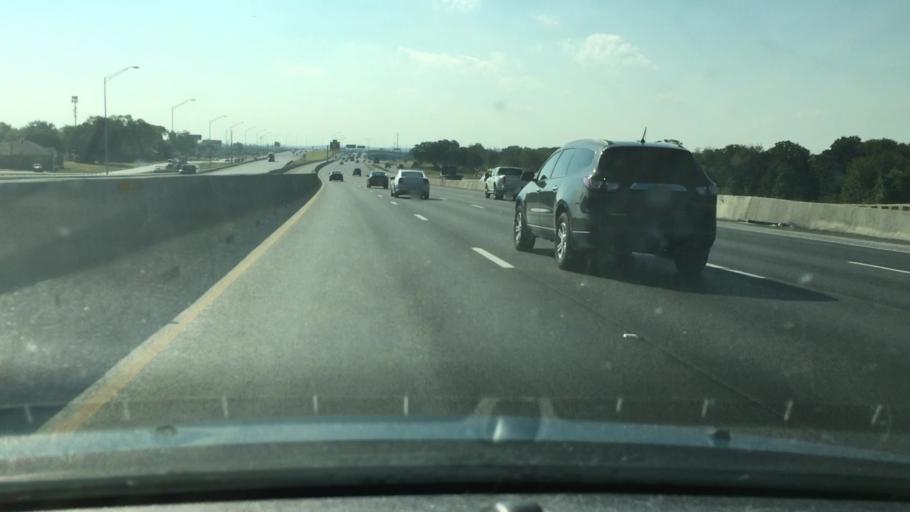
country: US
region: Texas
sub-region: Denton County
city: Lake Dallas
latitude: 33.1208
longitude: -97.0336
